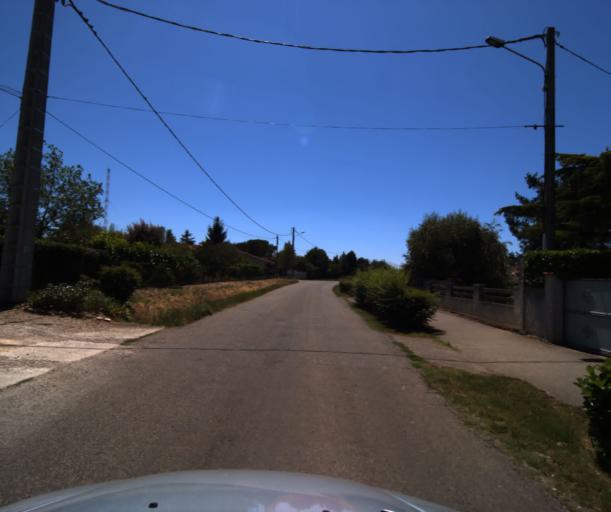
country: FR
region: Midi-Pyrenees
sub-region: Departement de la Haute-Garonne
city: Muret
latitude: 43.4549
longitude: 1.3401
